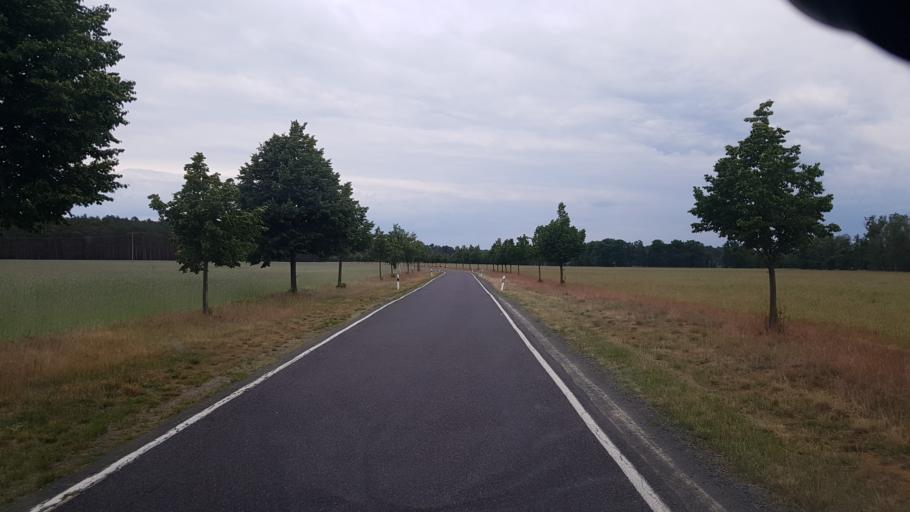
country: DE
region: Brandenburg
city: Herzberg
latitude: 51.7941
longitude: 13.2415
